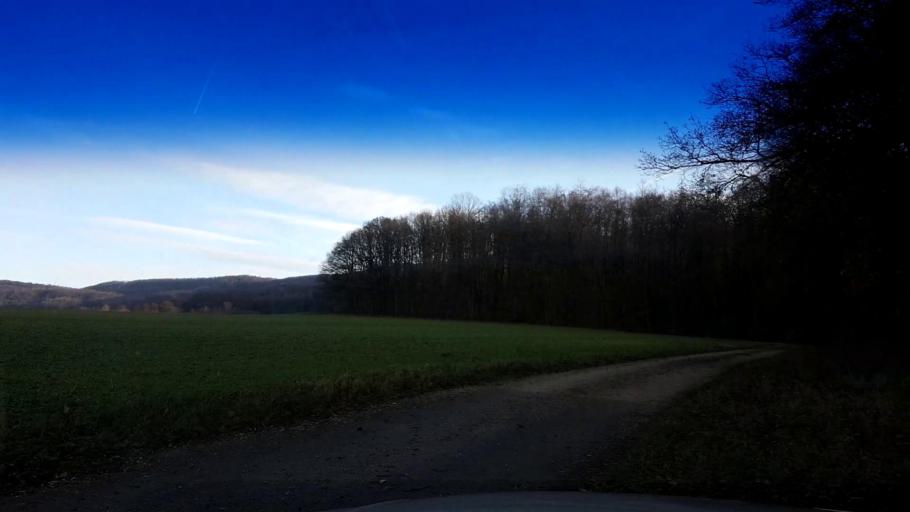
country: DE
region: Bavaria
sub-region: Upper Franconia
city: Schesslitz
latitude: 49.9447
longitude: 11.0304
